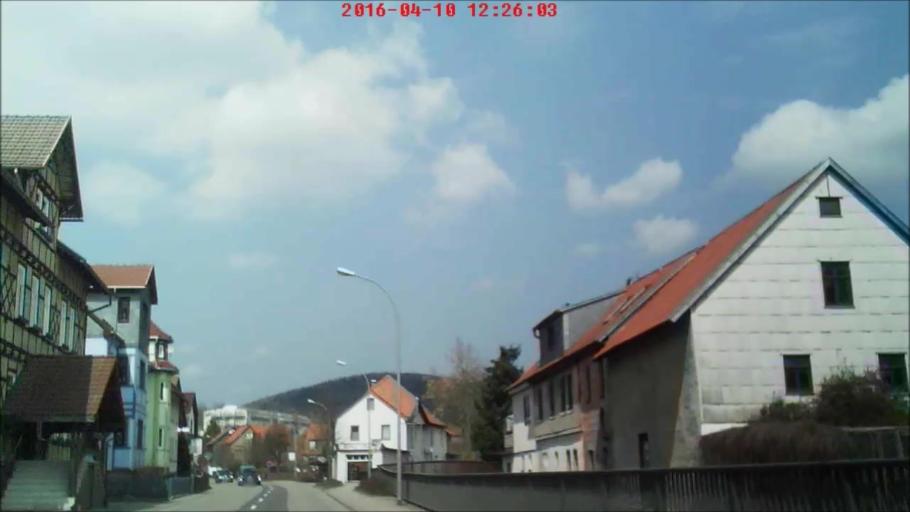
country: DE
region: Thuringia
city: Steinbach-Hallenberg
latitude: 50.6824
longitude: 10.5573
